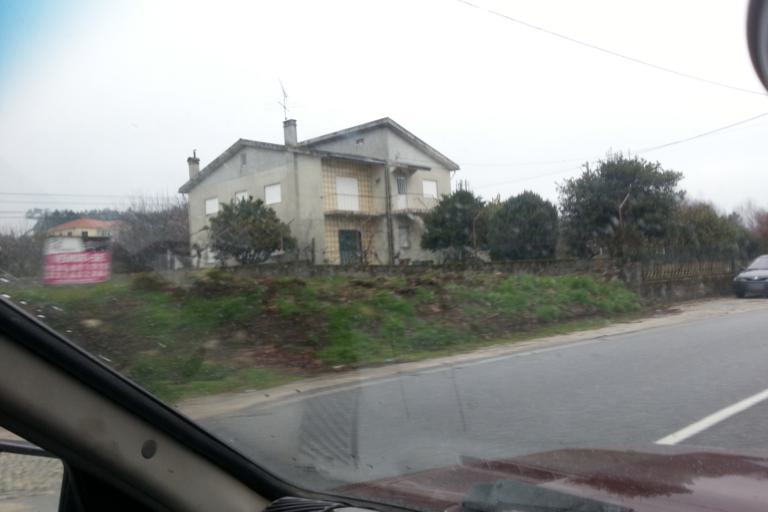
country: PT
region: Viseu
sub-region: Mangualde
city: Mangualde
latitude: 40.6079
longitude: -7.7351
